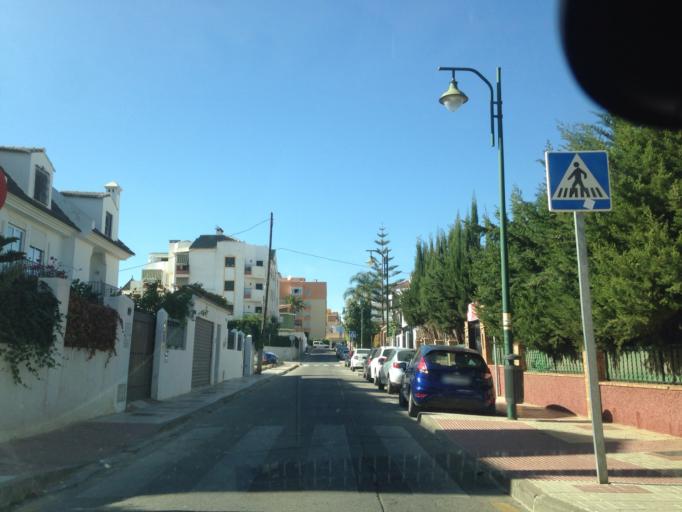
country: ES
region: Andalusia
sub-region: Provincia de Malaga
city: Malaga
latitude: 36.7218
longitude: -4.4518
